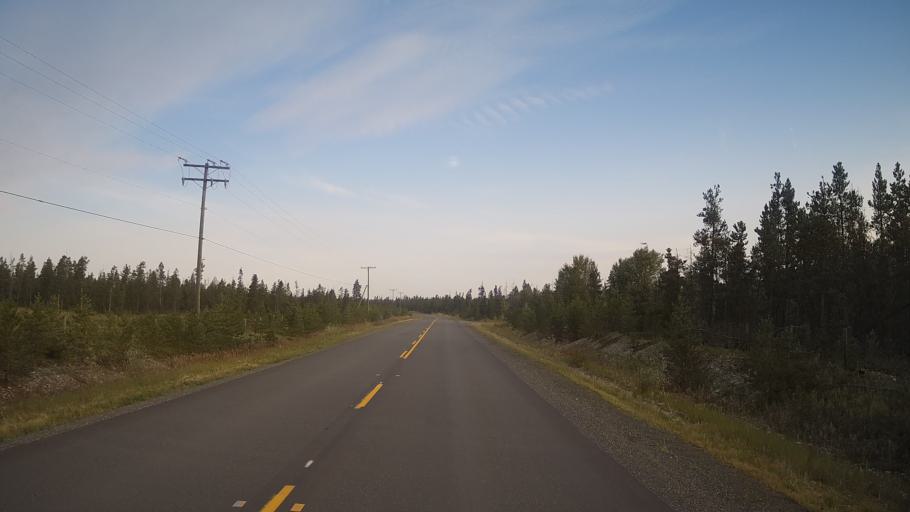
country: CA
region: British Columbia
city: Hanceville
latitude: 52.1339
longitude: -123.6999
